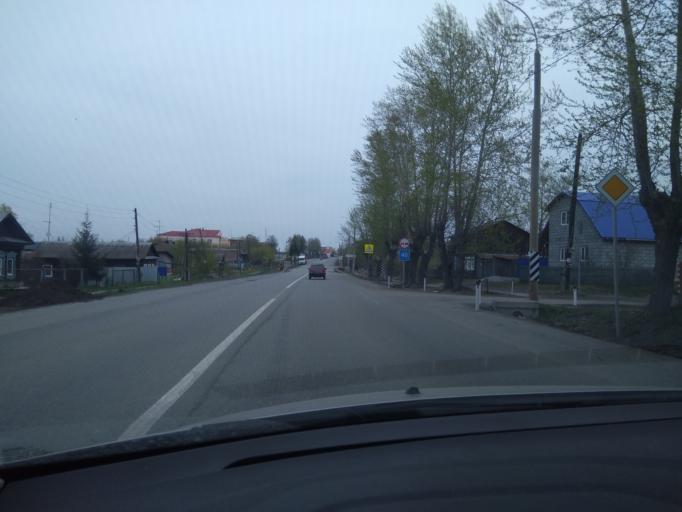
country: RU
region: Sverdlovsk
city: Beloyarskiy
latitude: 56.7588
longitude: 61.4087
